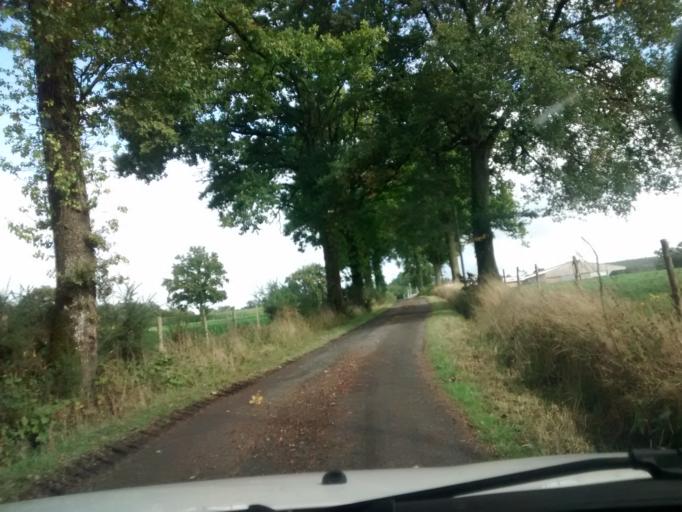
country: FR
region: Brittany
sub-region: Departement d'Ille-et-Vilaine
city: Chateaubourg
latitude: 48.1408
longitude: -1.4249
